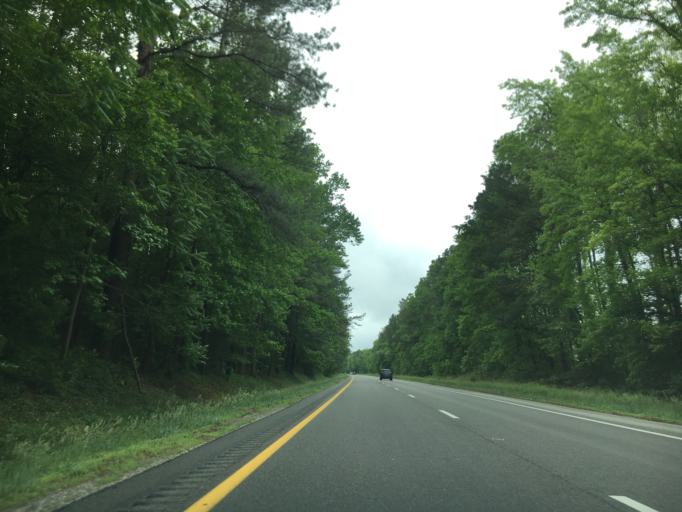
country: US
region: Virginia
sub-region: Brunswick County
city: Lawrenceville
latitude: 36.9049
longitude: -77.7892
